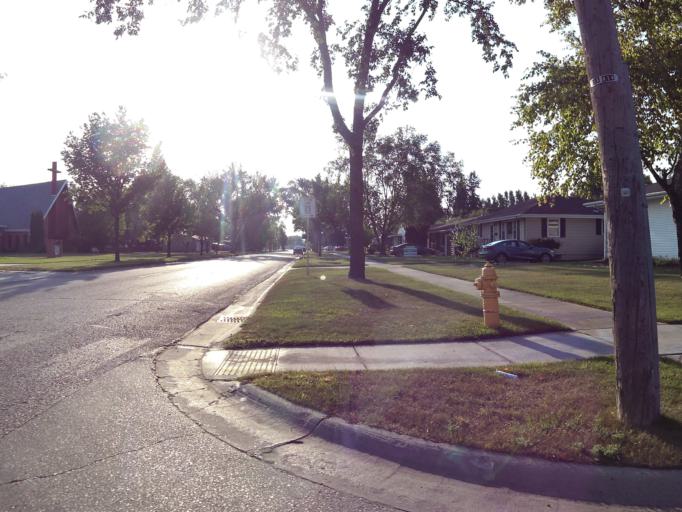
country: US
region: North Dakota
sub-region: Grand Forks County
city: Grand Forks
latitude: 47.8968
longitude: -97.0406
